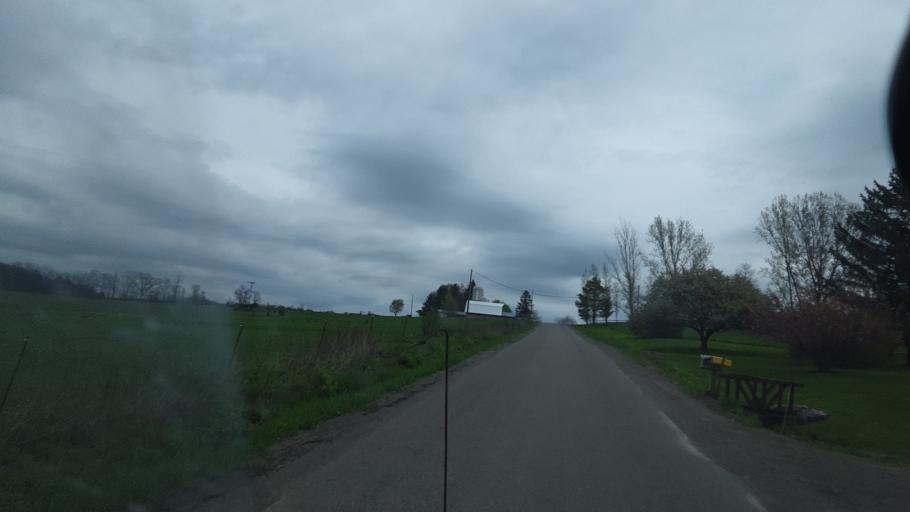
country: US
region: New York
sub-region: Steuben County
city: Addison
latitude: 42.0925
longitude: -77.2943
